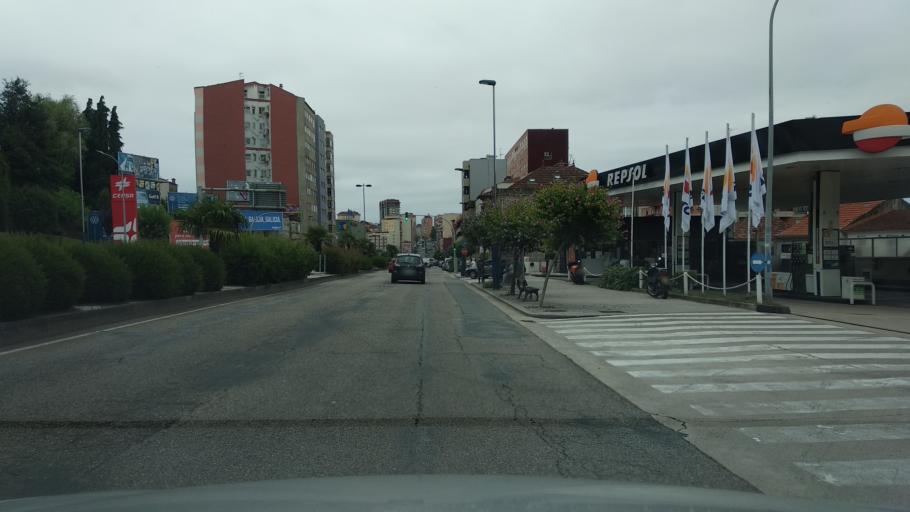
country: ES
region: Galicia
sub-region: Provincia de Pontevedra
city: Vigo
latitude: 42.2467
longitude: -8.6928
